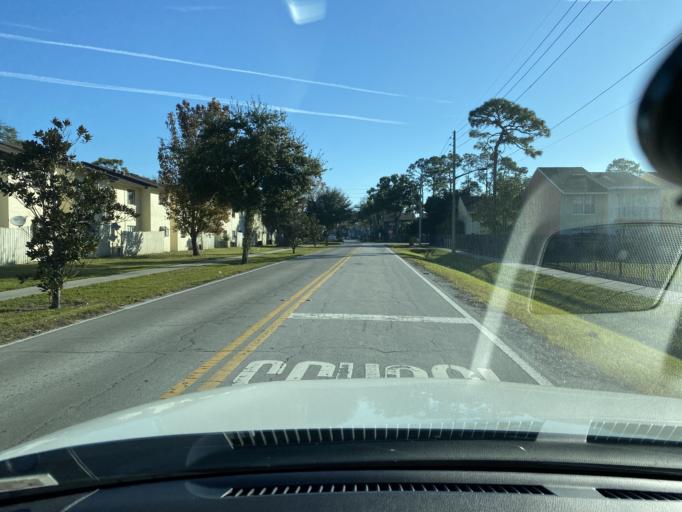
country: US
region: Florida
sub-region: Orange County
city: Azalea Park
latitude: 28.5331
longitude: -81.3075
